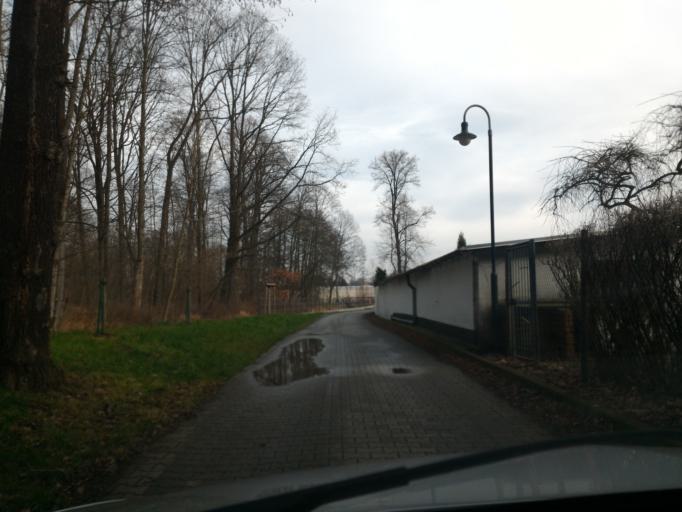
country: DE
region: Saxony
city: Grossschonau
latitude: 50.8935
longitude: 14.6560
